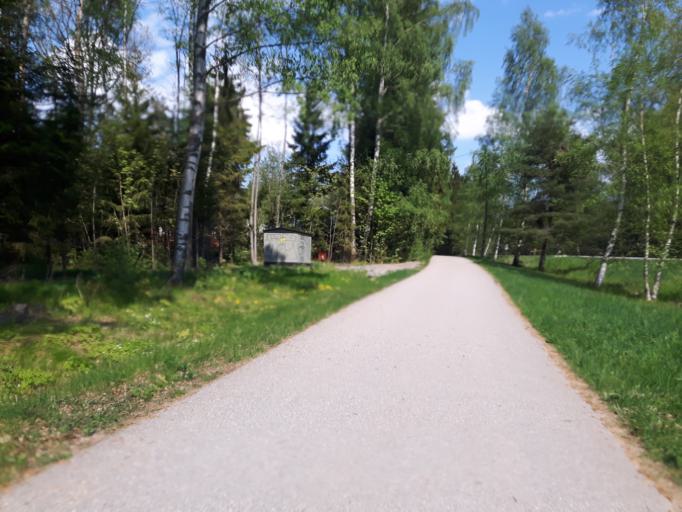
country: FI
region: Uusimaa
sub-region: Porvoo
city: Porvoo
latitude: 60.3855
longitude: 25.6265
